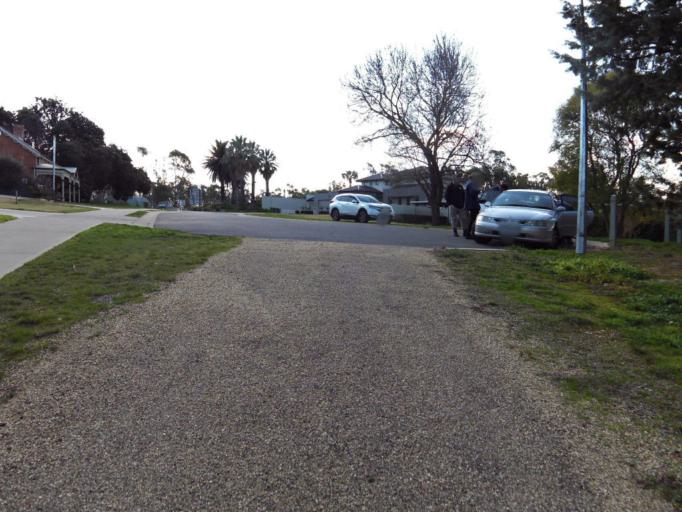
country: AU
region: New South Wales
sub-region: Corowa Shire
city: Corowa
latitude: -36.0083
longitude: 146.3957
